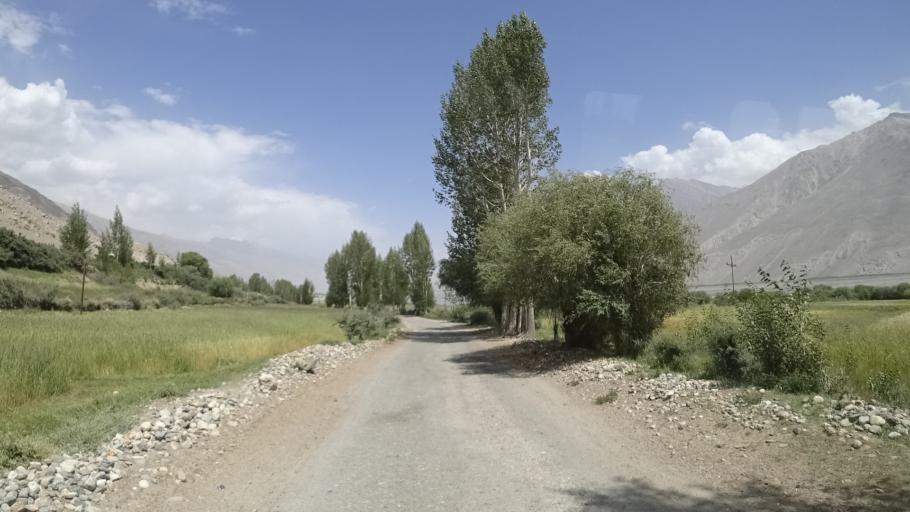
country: AF
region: Badakhshan
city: Khandud
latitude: 36.9251
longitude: 72.1976
